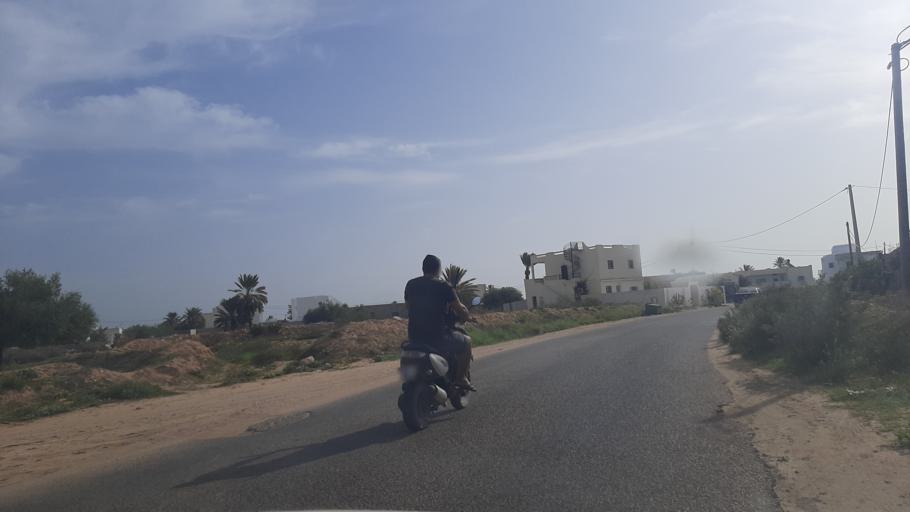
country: TN
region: Madanin
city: Midoun
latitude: 33.7955
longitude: 11.0297
